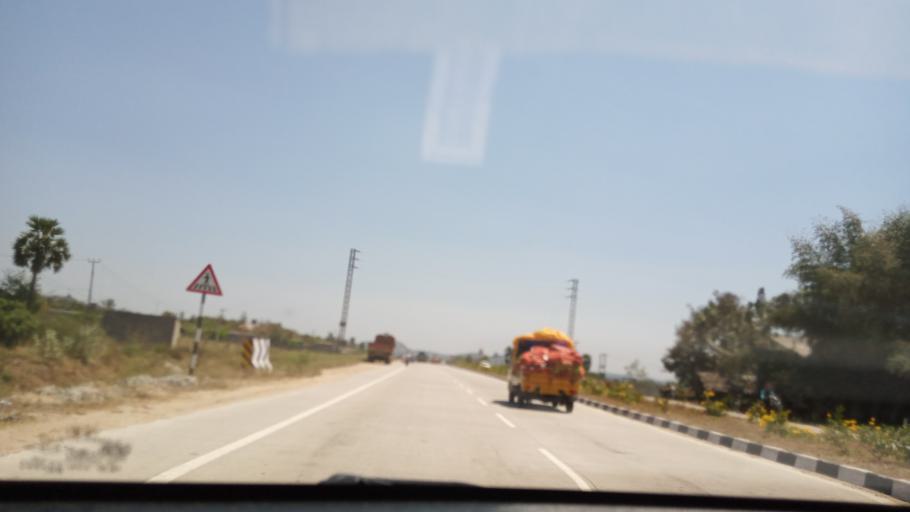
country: IN
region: Andhra Pradesh
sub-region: Chittoor
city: Chittoor
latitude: 13.1941
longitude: 79.0280
